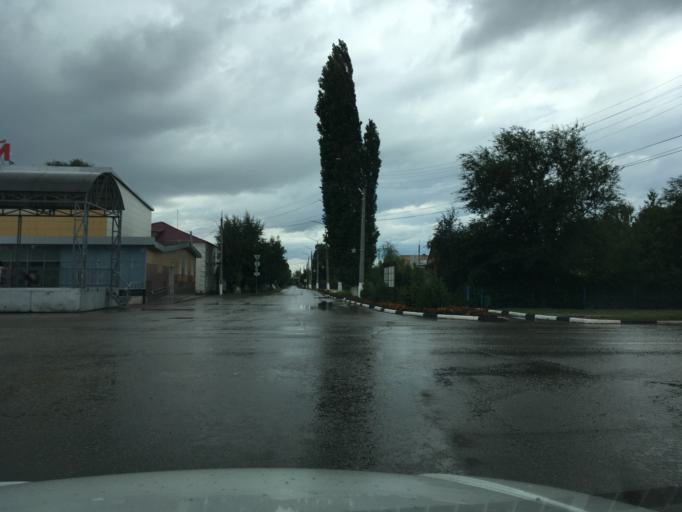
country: RU
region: Samara
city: Bezenchuk
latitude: 52.9837
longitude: 49.4397
